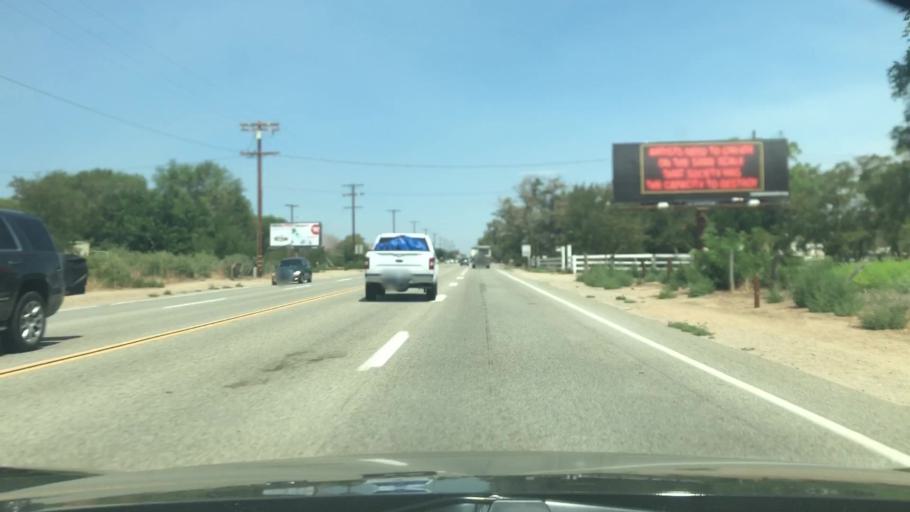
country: US
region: California
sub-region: Inyo County
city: Lone Pine
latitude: 36.5958
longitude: -118.0585
